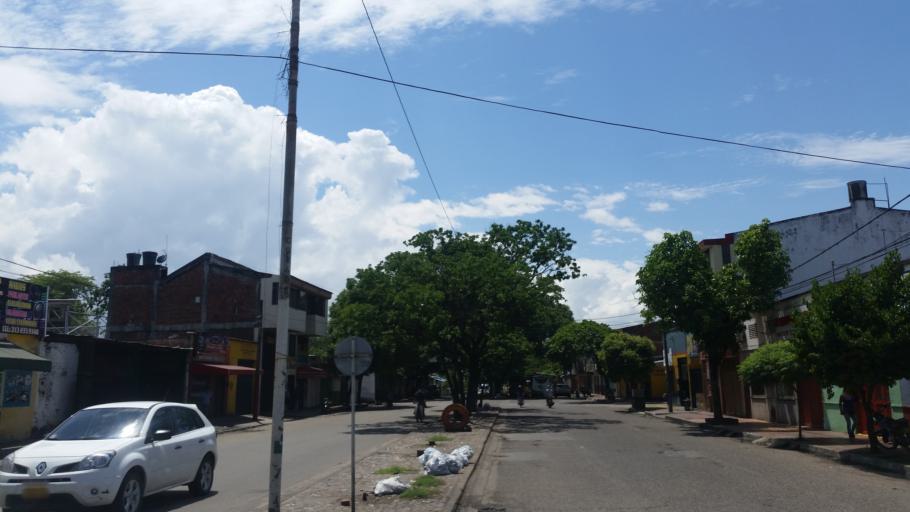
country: CO
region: Huila
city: Neiva
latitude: 2.9225
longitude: -75.2851
